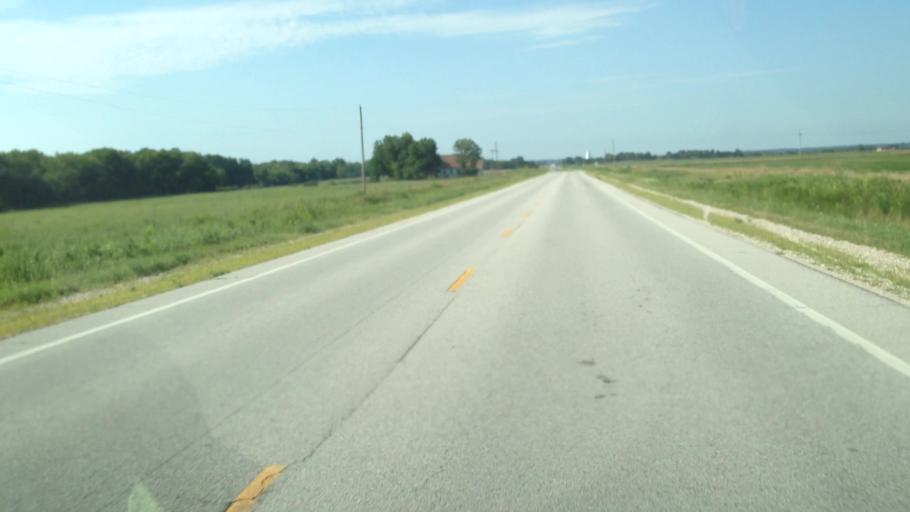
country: US
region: Kansas
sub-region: Neosho County
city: Erie
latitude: 37.4823
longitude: -95.2693
